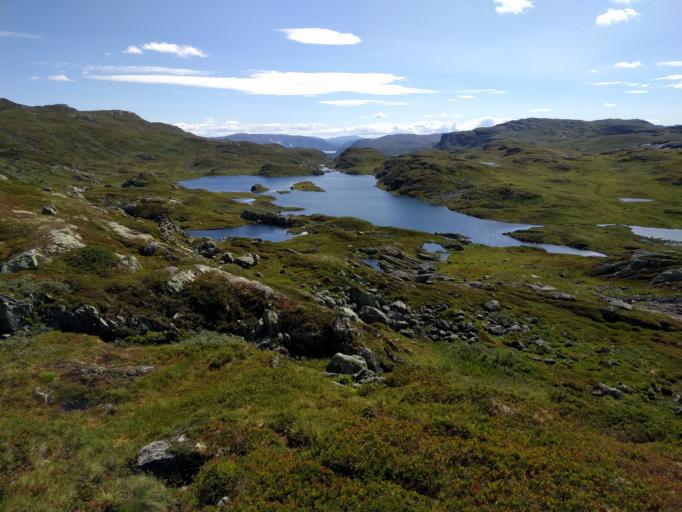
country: NO
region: Aust-Agder
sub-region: Bykle
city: Hovden
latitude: 59.8434
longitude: 7.2063
